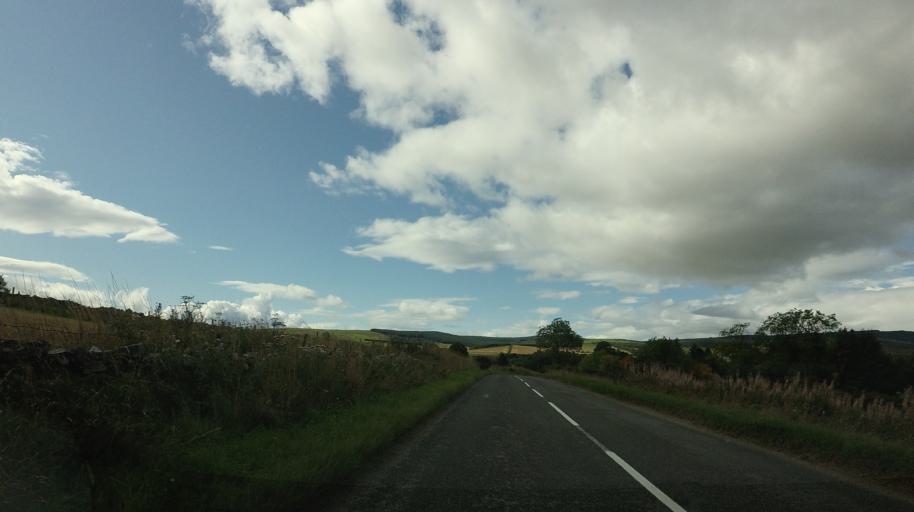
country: GB
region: Scotland
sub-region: Aberdeenshire
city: Alford
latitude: 57.2343
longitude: -2.7364
